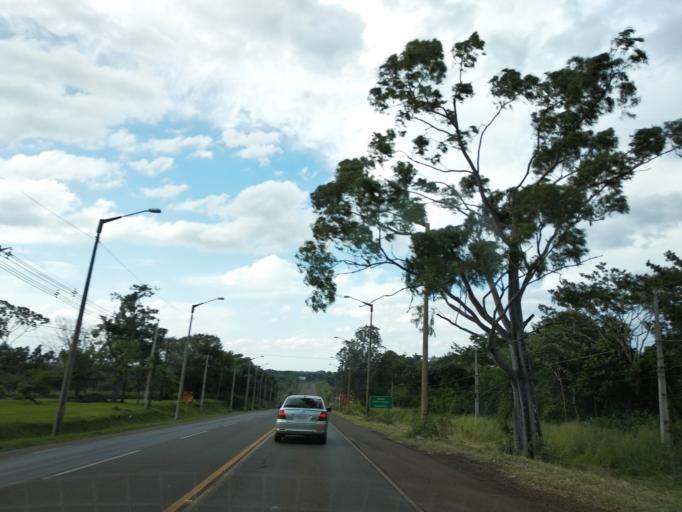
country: PY
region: Itapua
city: San Juan del Parana
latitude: -27.2926
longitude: -55.9248
